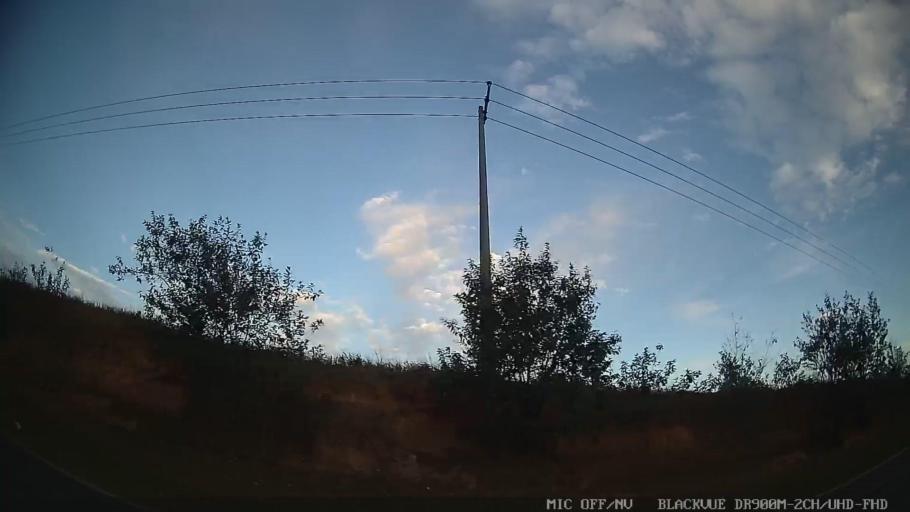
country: BR
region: Sao Paulo
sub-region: Salto
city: Salto
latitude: -23.1603
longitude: -47.2628
